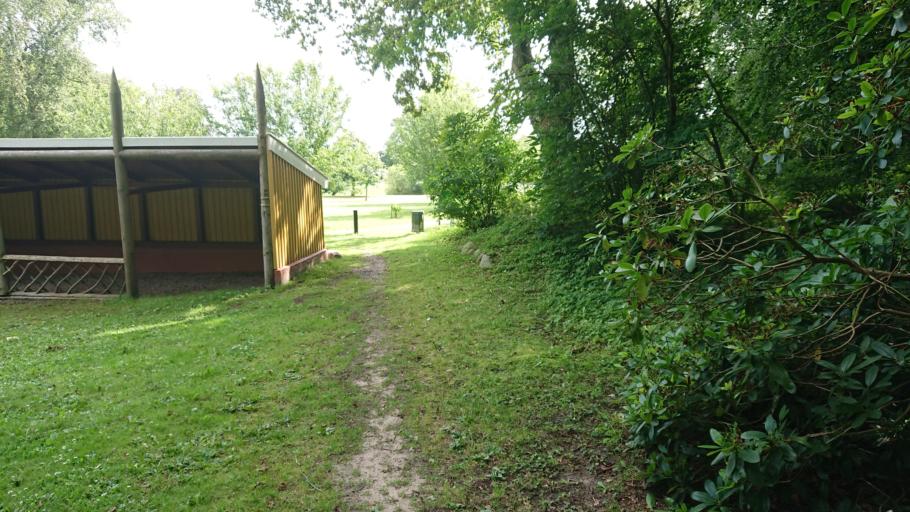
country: DK
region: North Denmark
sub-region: Frederikshavn Kommune
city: Saeby
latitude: 57.3393
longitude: 10.5103
